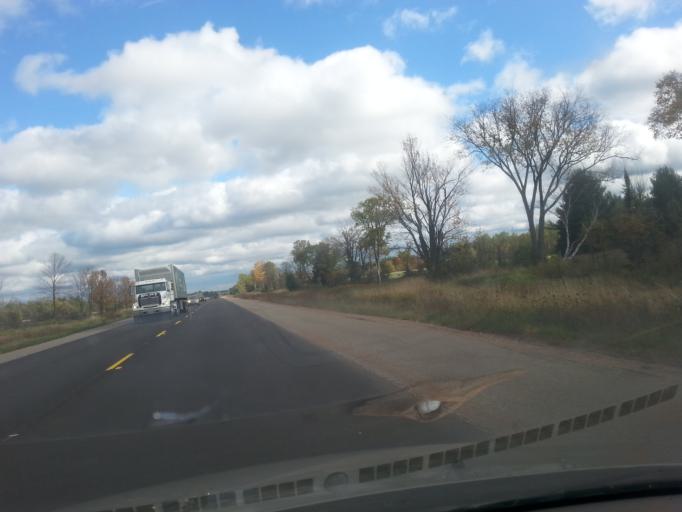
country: CA
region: Ontario
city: Pembroke
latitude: 45.7929
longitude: -77.1609
